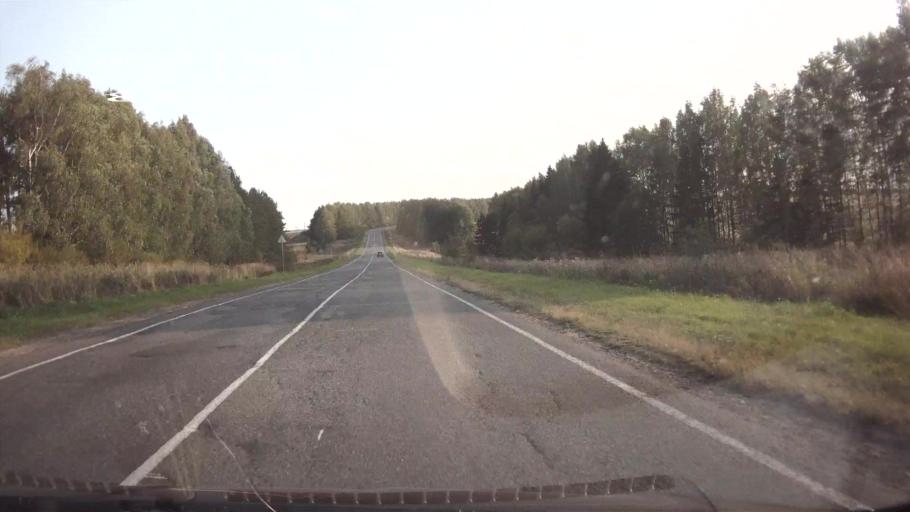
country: RU
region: Mariy-El
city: Kuzhener
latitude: 56.8648
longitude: 48.7560
